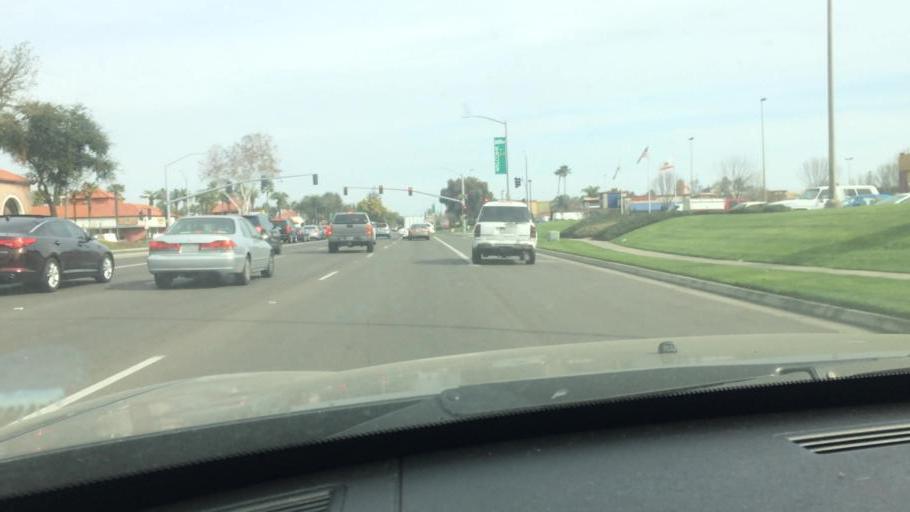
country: US
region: California
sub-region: Fresno County
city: Tarpey Village
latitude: 36.8083
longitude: -119.6964
